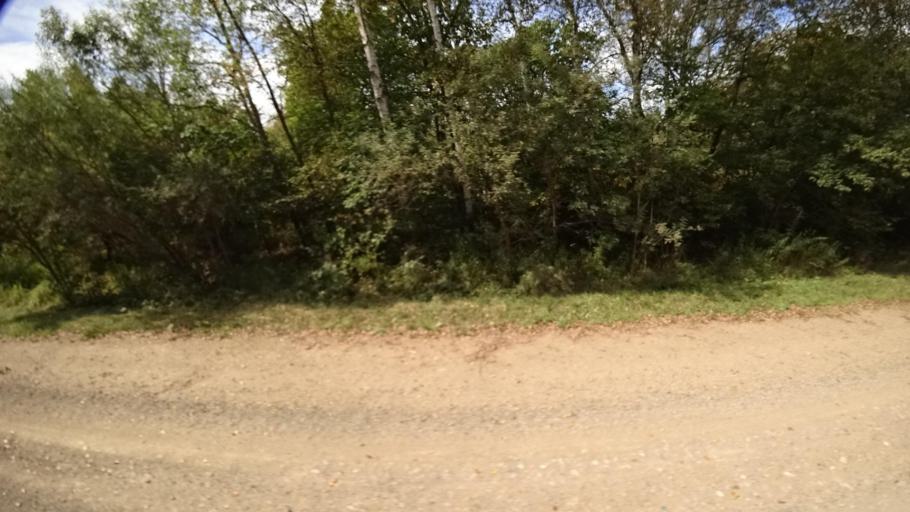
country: RU
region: Primorskiy
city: Yakovlevka
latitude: 44.6939
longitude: 133.6193
